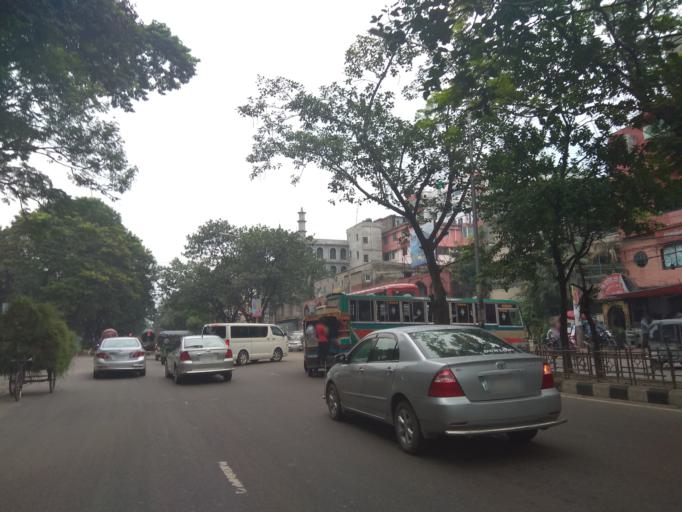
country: BD
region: Dhaka
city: Azimpur
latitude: 23.7612
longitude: 90.3835
